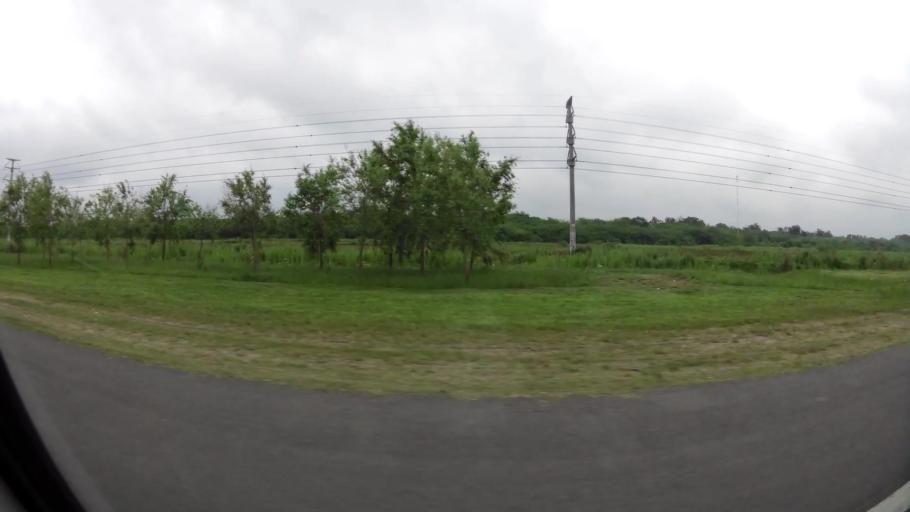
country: AR
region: Buenos Aires
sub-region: Partido de La Plata
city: La Plata
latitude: -34.8236
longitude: -58.0989
